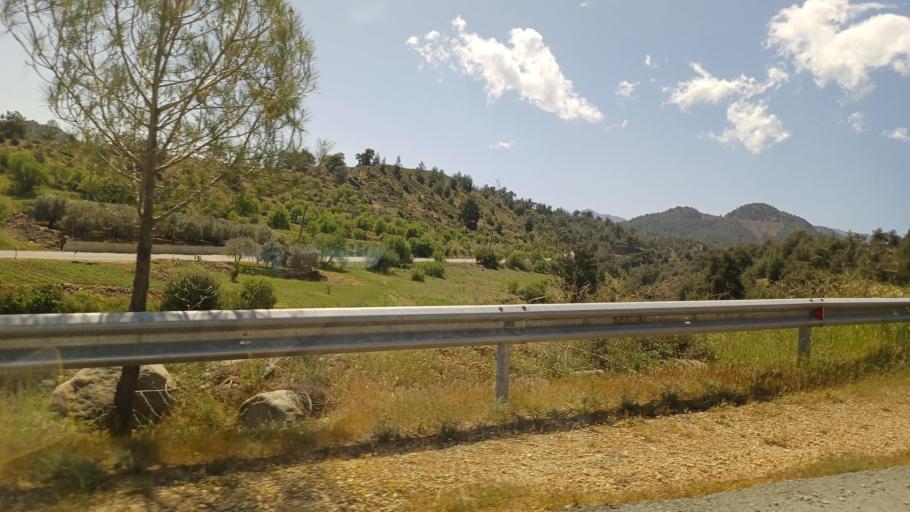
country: CY
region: Lefkosia
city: Astromeritis
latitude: 35.0562
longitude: 33.0267
